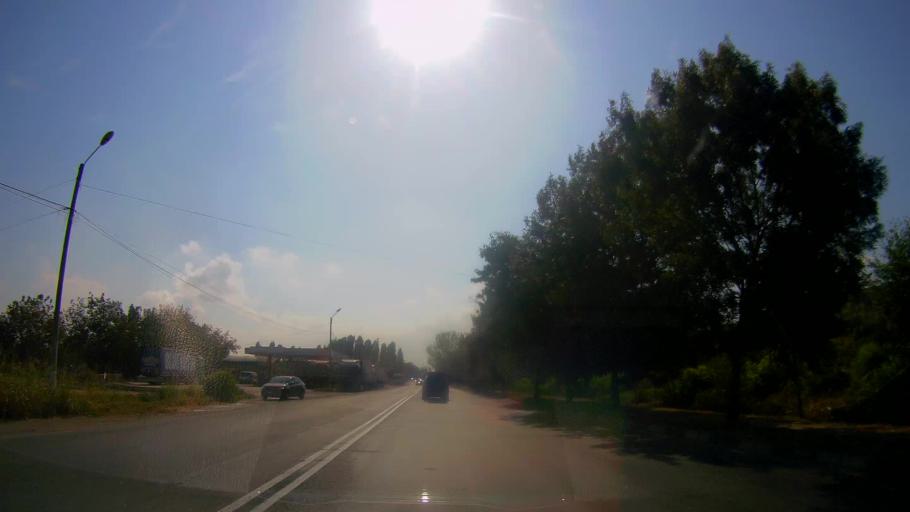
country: RO
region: Giurgiu
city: Giurgiu
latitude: 43.9105
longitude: 25.9771
